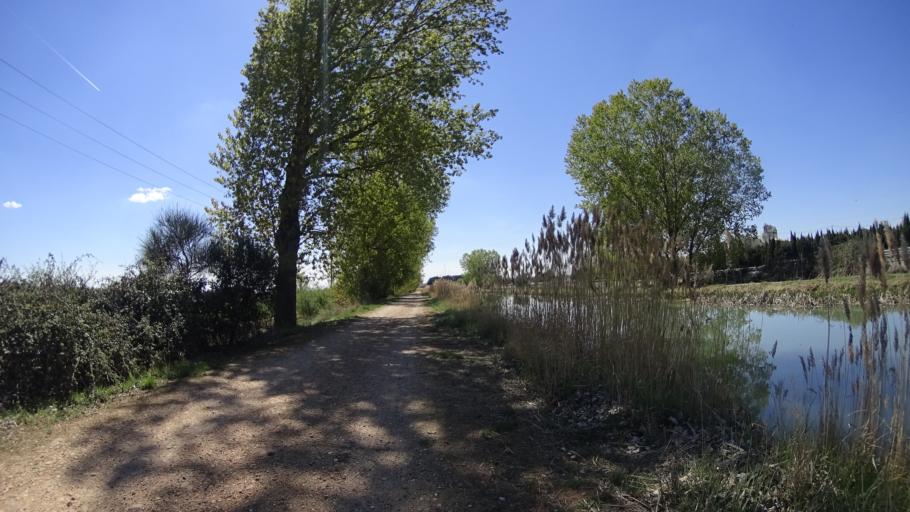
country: ES
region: Castille and Leon
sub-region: Provincia de Valladolid
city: Cabezon
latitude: 41.7364
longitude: -4.6699
